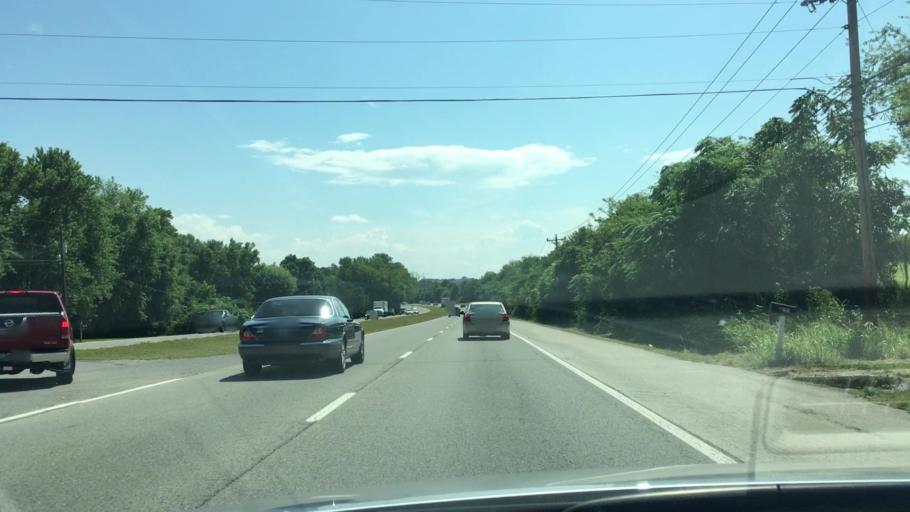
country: US
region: Tennessee
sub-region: Maury County
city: Columbia
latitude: 35.6878
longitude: -86.9941
